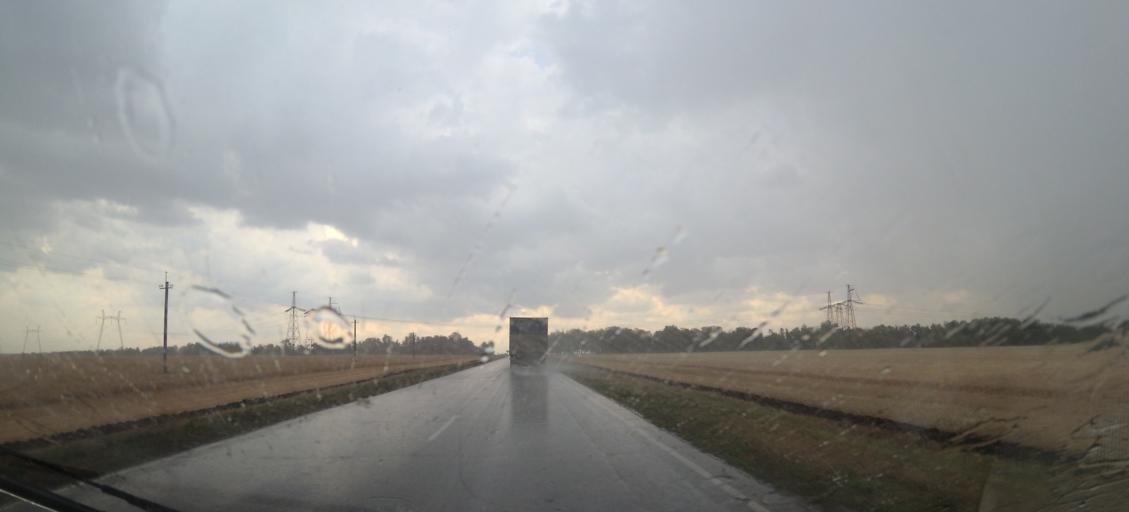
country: RU
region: Rostov
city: Gundorovskiy
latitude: 46.8619
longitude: 41.9518
